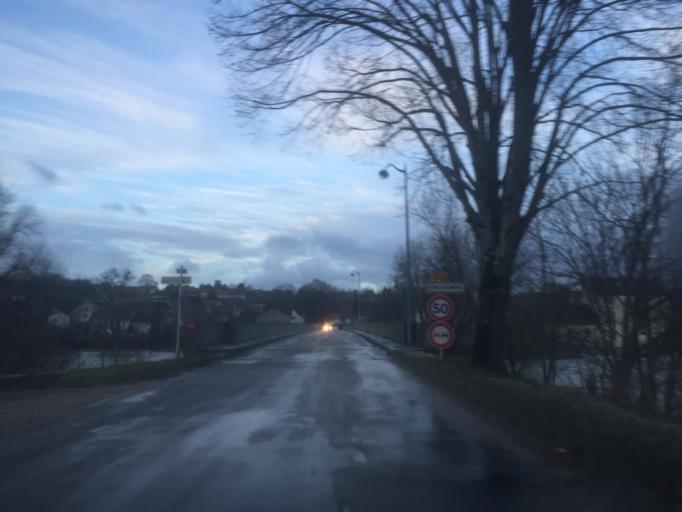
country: FR
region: Franche-Comte
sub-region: Departement du Jura
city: Orchamps
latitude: 47.1442
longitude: 5.6559
